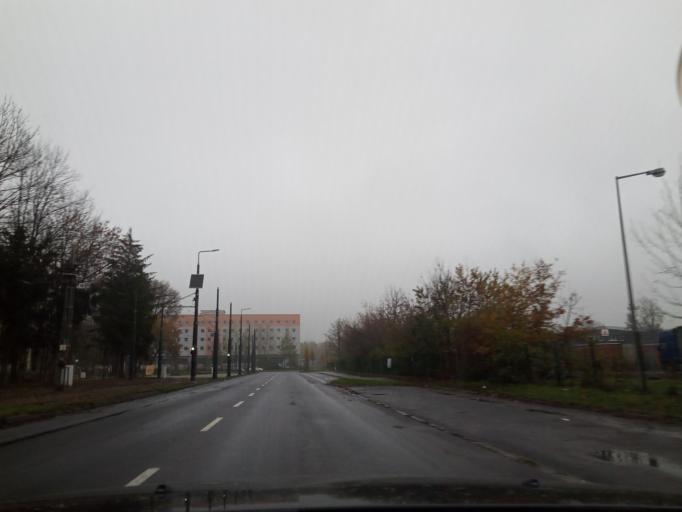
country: PL
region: Lesser Poland Voivodeship
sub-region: Powiat wielicki
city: Kokotow
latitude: 50.0863
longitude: 20.0655
